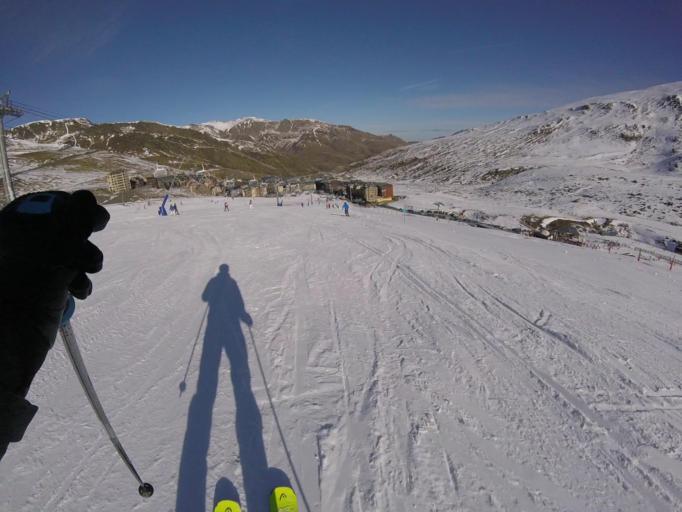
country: AD
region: Encamp
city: Pas de la Casa
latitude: 42.5359
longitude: 1.7310
